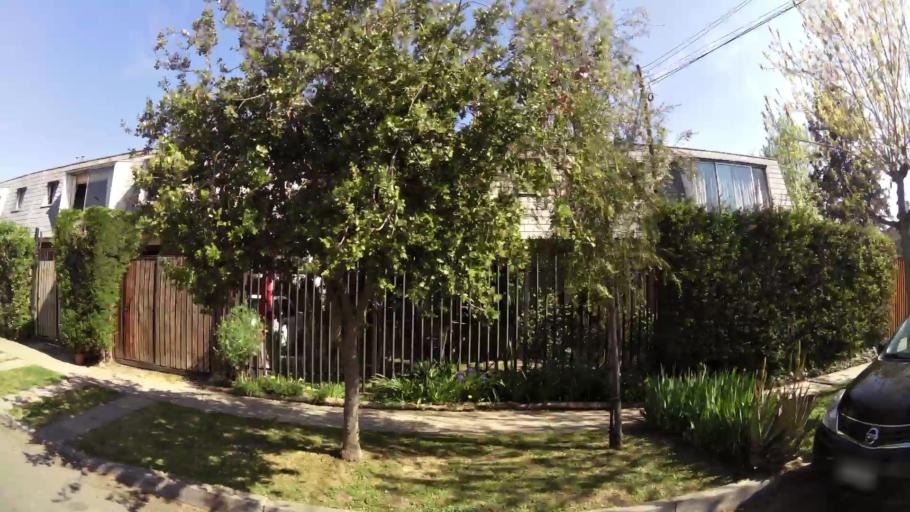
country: CL
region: Santiago Metropolitan
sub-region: Provincia de Santiago
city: Villa Presidente Frei, Nunoa, Santiago, Chile
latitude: -33.4961
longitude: -70.5776
